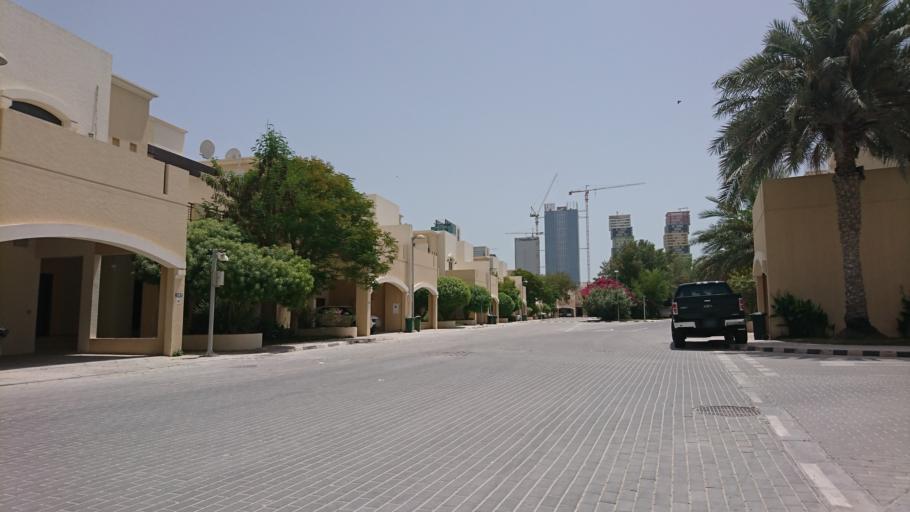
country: QA
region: Baladiyat ad Dawhah
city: Doha
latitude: 25.3851
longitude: 51.5142
